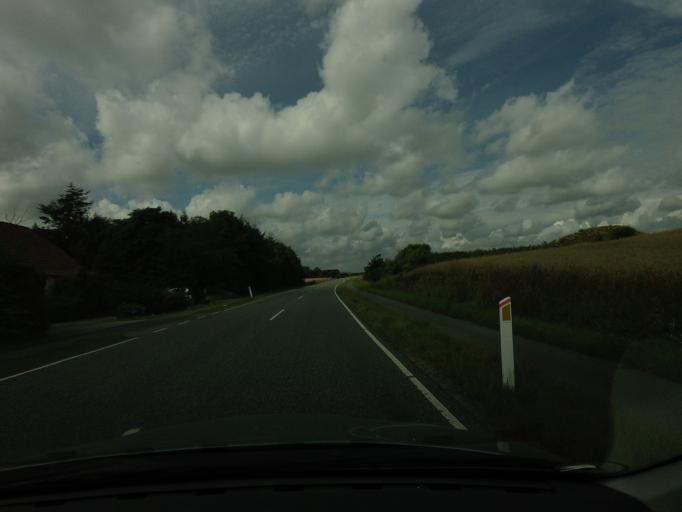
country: DK
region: North Denmark
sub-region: Hjorring Kommune
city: Sindal
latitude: 57.3415
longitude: 10.2671
